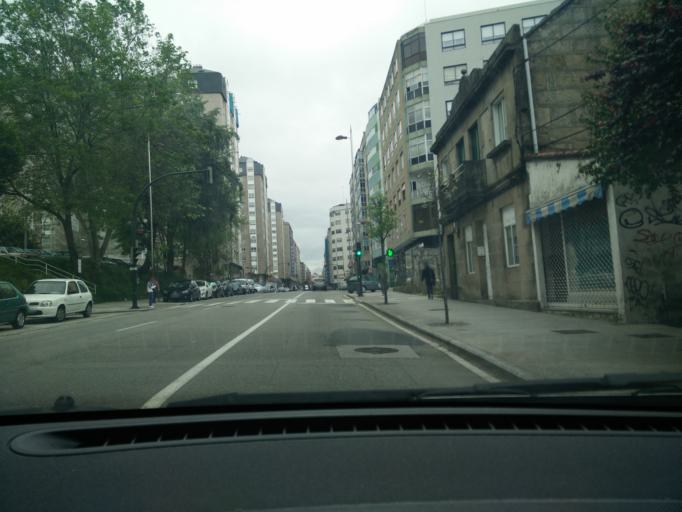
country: ES
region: Galicia
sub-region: Provincia de Pontevedra
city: Vigo
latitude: 42.2135
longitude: -8.7433
